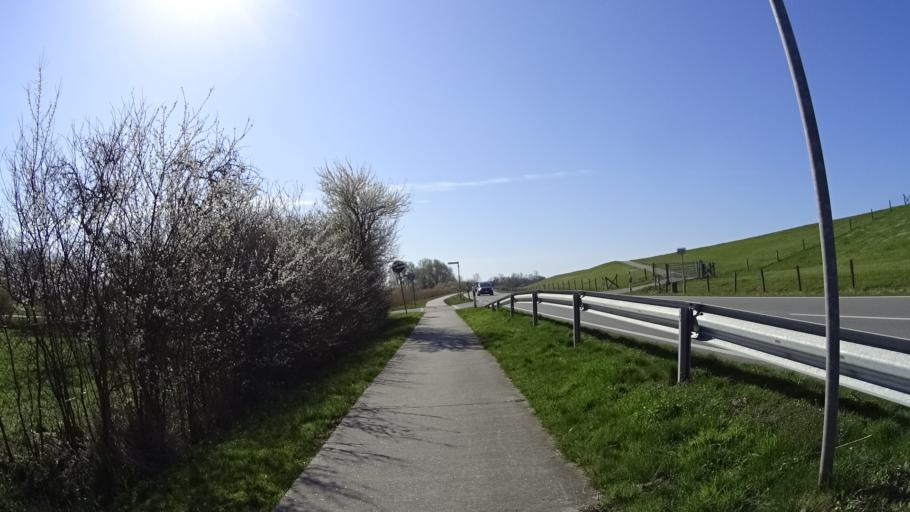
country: DE
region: Lower Saxony
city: Jemgum
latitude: 53.2789
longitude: 7.4064
